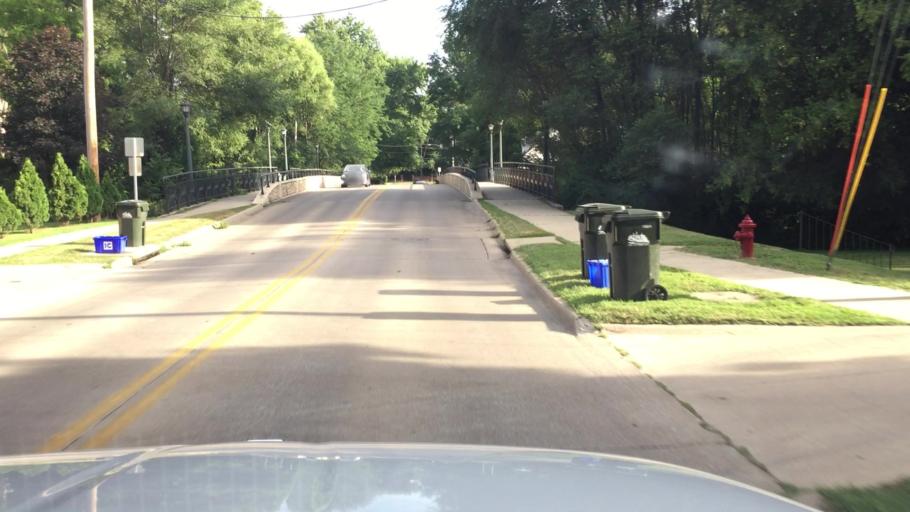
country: US
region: Iowa
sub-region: Johnson County
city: Iowa City
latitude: 41.6518
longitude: -91.5212
